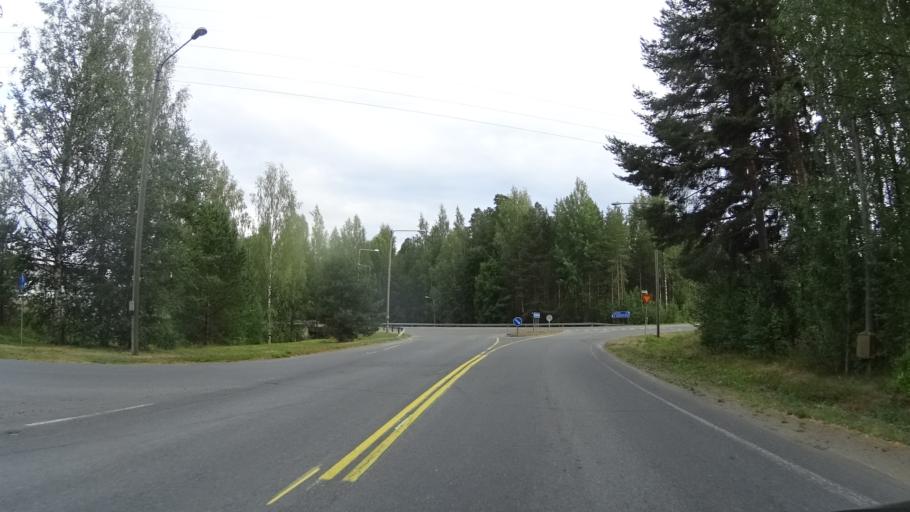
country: FI
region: Haeme
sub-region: Haemeenlinna
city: Parola
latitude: 61.0142
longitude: 24.3871
